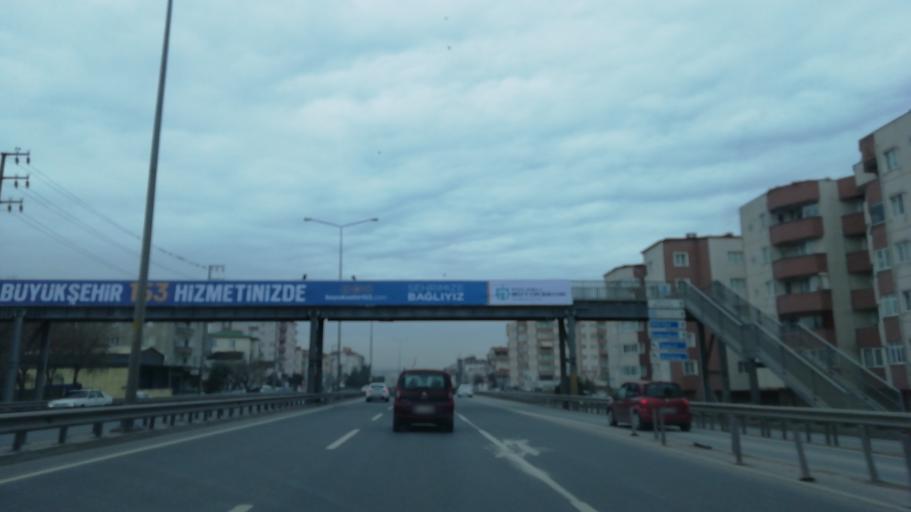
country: TR
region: Kocaeli
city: Derince
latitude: 40.7562
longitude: 29.8230
